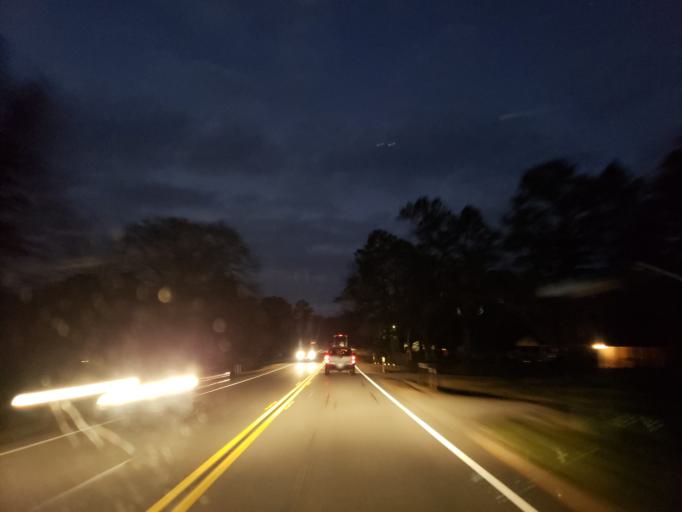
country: US
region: Georgia
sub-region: Polk County
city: Rockmart
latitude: 33.9380
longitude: -84.9970
